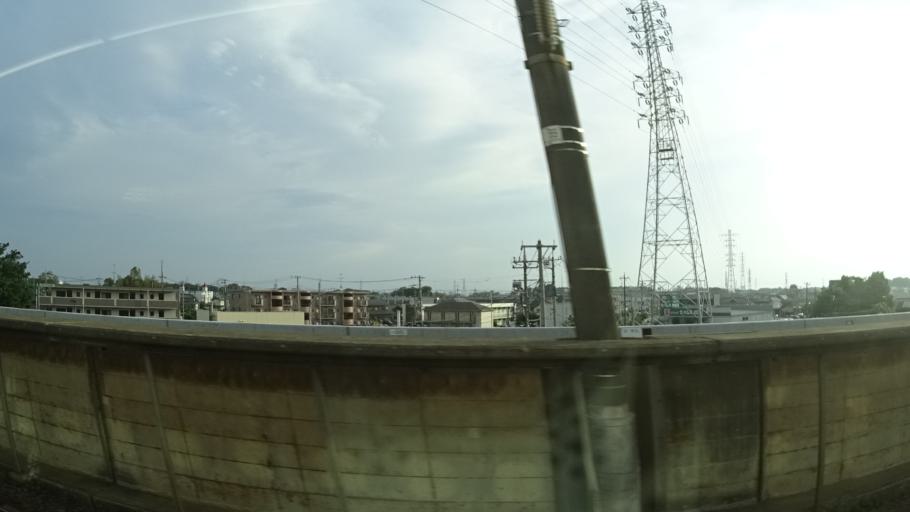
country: JP
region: Saitama
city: Ageoshimo
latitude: 36.0088
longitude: 139.6070
